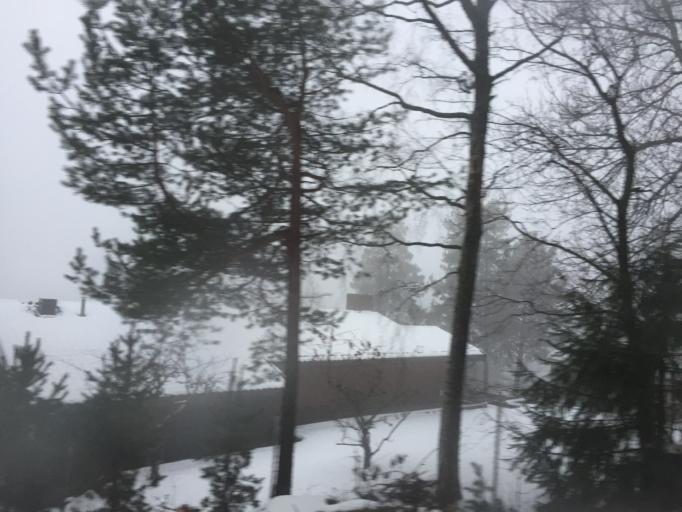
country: NO
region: Oslo
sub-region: Oslo
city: Sjolyststranda
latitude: 59.9592
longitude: 10.6660
